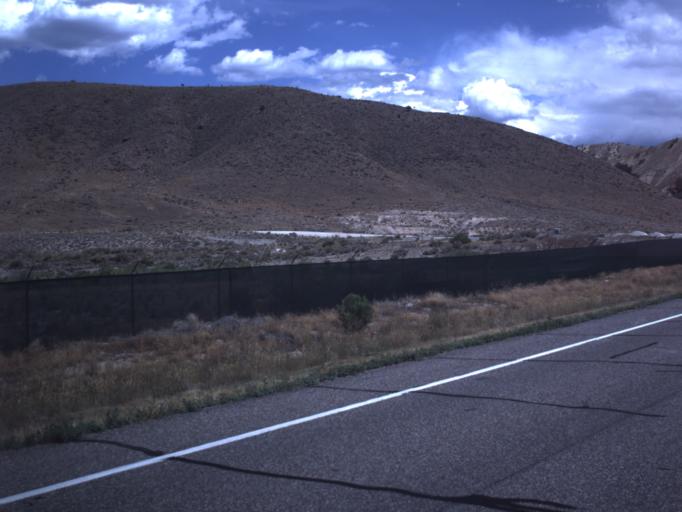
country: US
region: Utah
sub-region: Sevier County
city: Aurora
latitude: 38.8322
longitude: -111.9650
